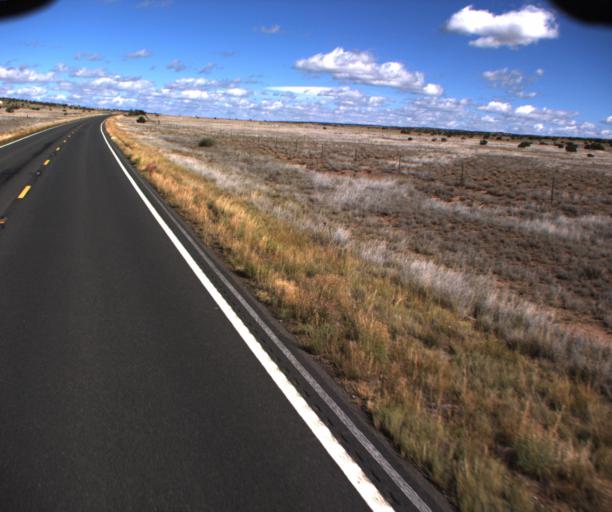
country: US
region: Arizona
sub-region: Apache County
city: Houck
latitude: 34.9236
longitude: -109.2382
